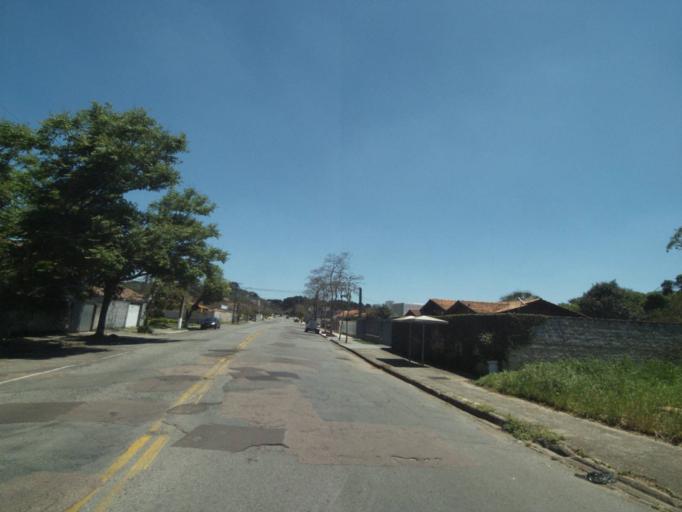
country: BR
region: Parana
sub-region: Pinhais
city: Pinhais
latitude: -25.3955
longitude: -49.2210
